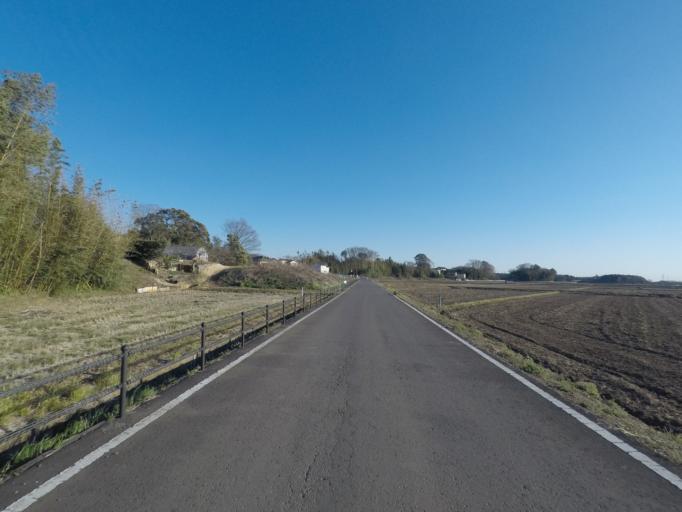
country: JP
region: Ibaraki
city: Ishige
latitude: 36.1459
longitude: 140.0084
